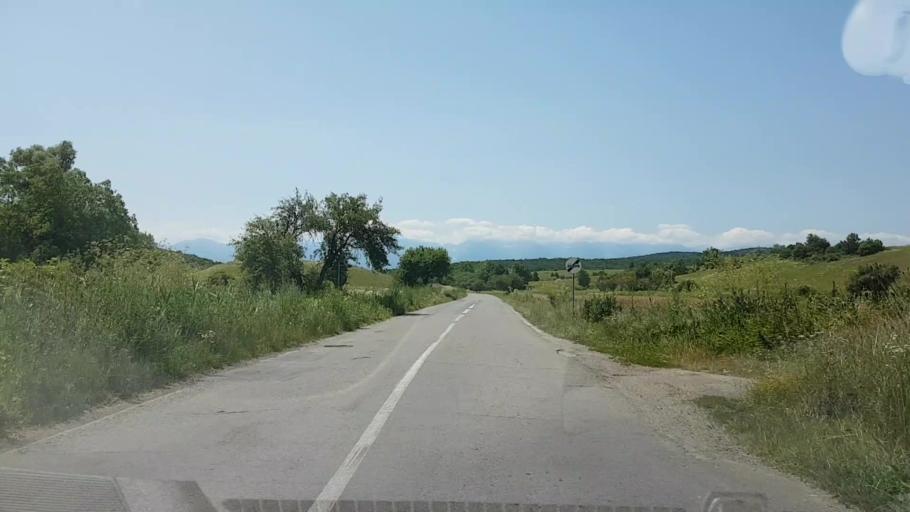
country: RO
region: Brasov
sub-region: Comuna Cincu
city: Cincu
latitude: 45.8969
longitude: 24.8120
